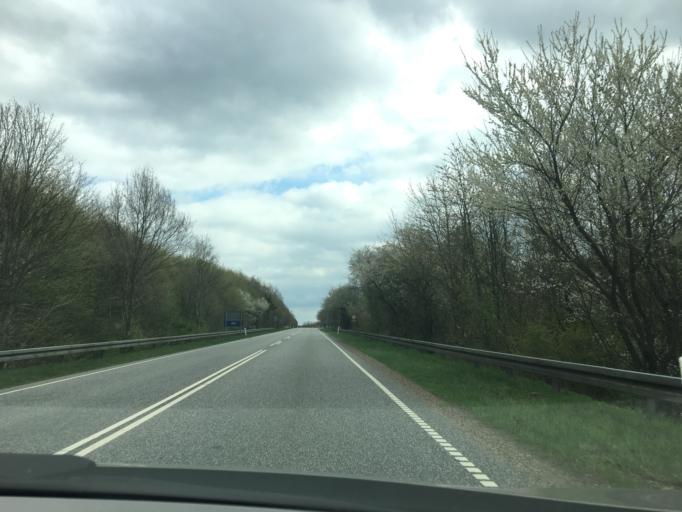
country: DK
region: Central Jutland
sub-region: Horsens Kommune
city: Braedstrup
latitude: 55.9656
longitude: 9.6060
